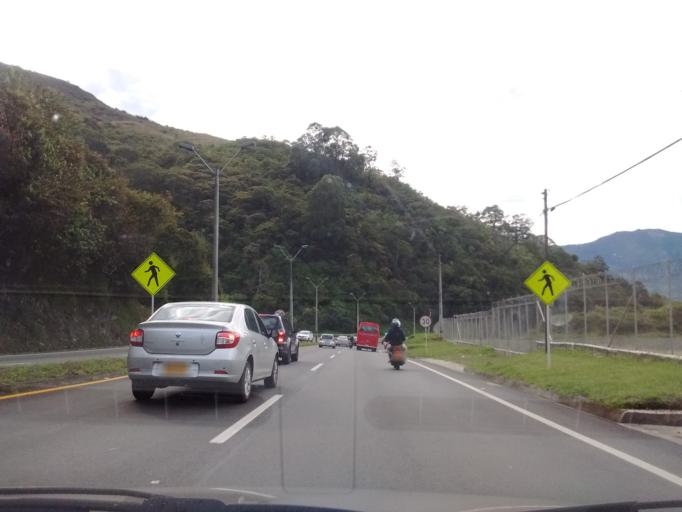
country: CO
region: Antioquia
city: Municipio de Copacabana
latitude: 6.3137
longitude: -75.5067
